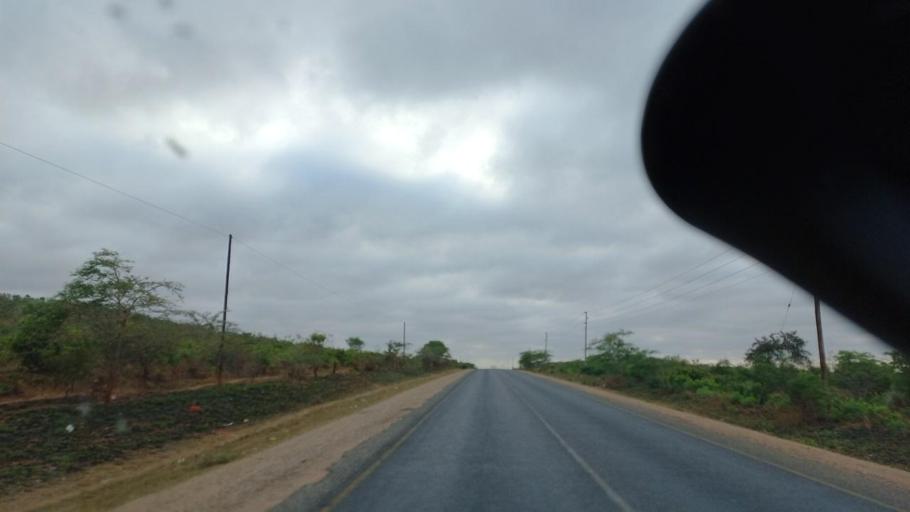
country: ZM
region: Lusaka
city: Chongwe
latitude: -15.3419
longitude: 28.5982
